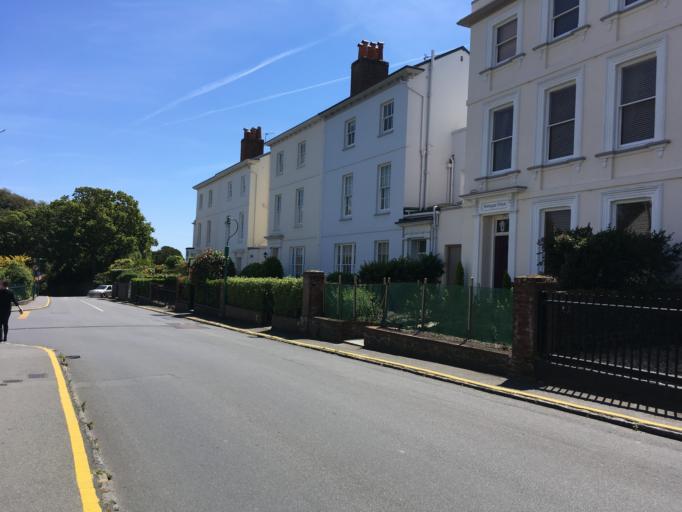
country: GG
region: St Peter Port
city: Saint Peter Port
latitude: 49.4594
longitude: -2.5430
